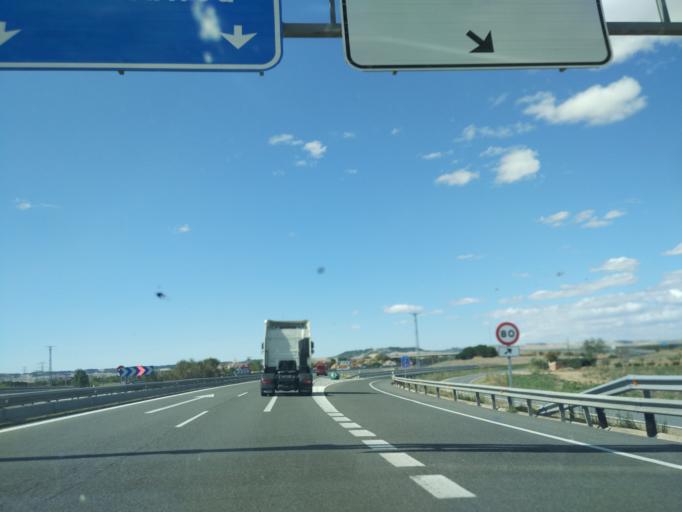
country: ES
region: Castille and Leon
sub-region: Provincia de Valladolid
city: Tordesillas
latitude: 41.4766
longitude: -4.9907
